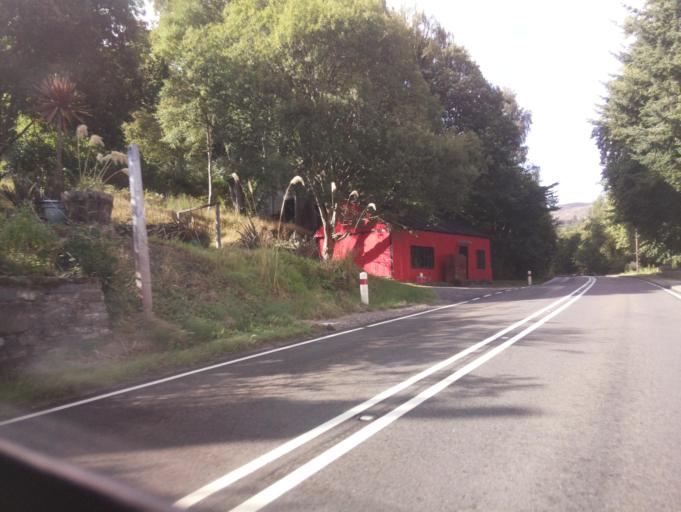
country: GB
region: Scotland
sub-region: Highland
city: Beauly
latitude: 57.2068
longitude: -4.6092
